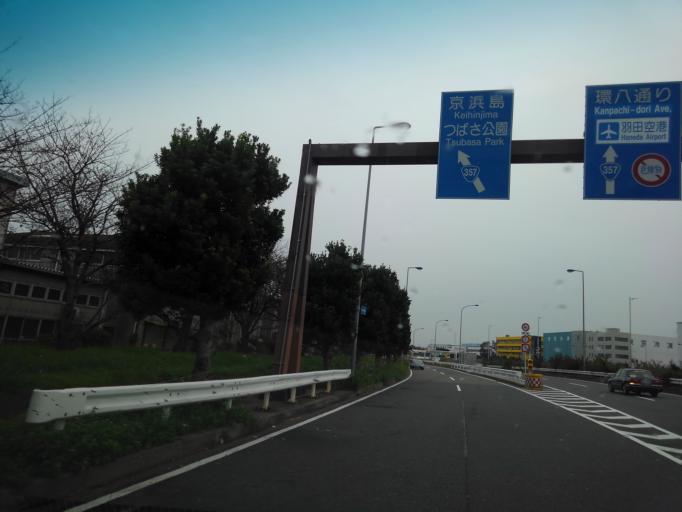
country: JP
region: Kanagawa
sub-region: Kawasaki-shi
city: Kawasaki
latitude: 35.5690
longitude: 139.7611
